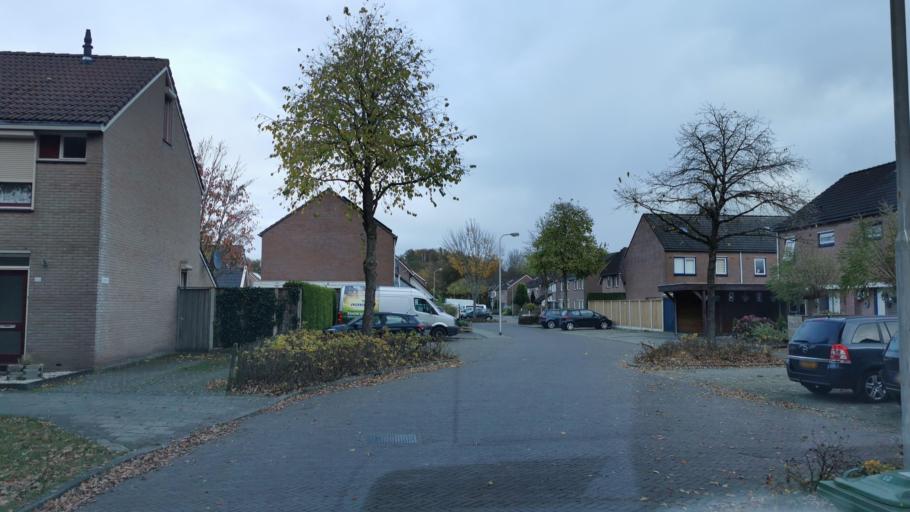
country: DE
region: North Rhine-Westphalia
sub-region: Regierungsbezirk Munster
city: Gronau
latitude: 52.2363
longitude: 7.0424
